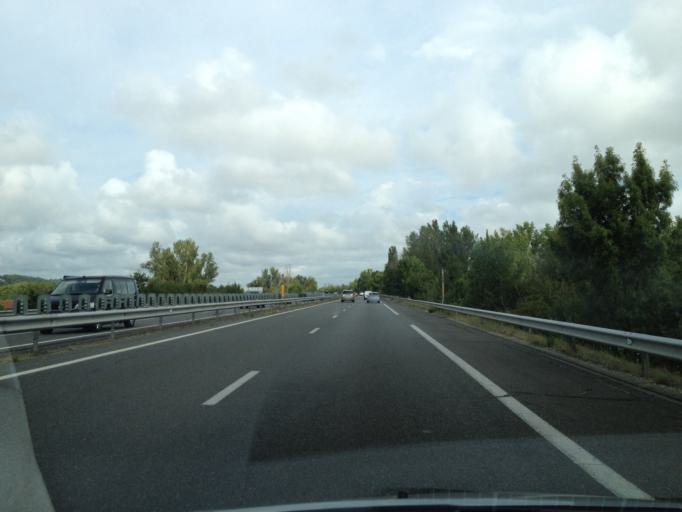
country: FR
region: Aquitaine
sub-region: Departement du Lot-et-Garonne
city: Layrac
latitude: 44.1374
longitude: 0.6719
